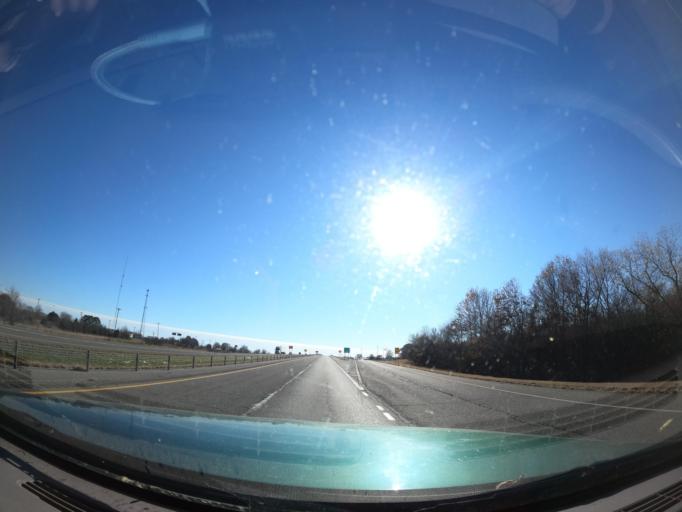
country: US
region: Oklahoma
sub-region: McIntosh County
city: Eufaula
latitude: 35.3655
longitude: -95.5733
